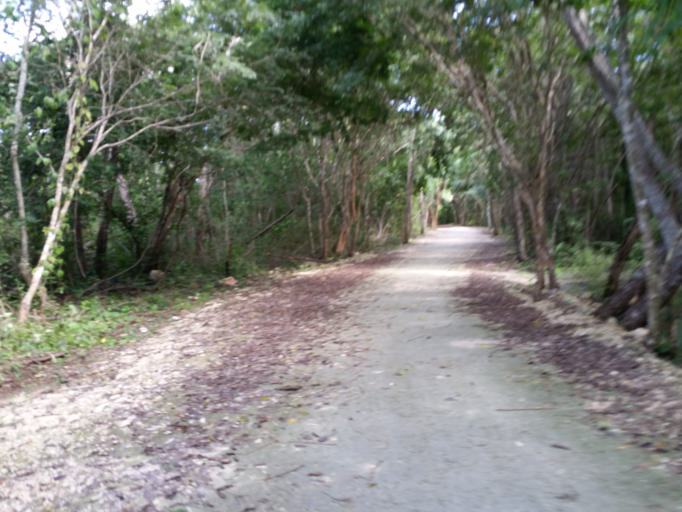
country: MX
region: Yucatan
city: Temozon
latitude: 20.8884
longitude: -88.1241
